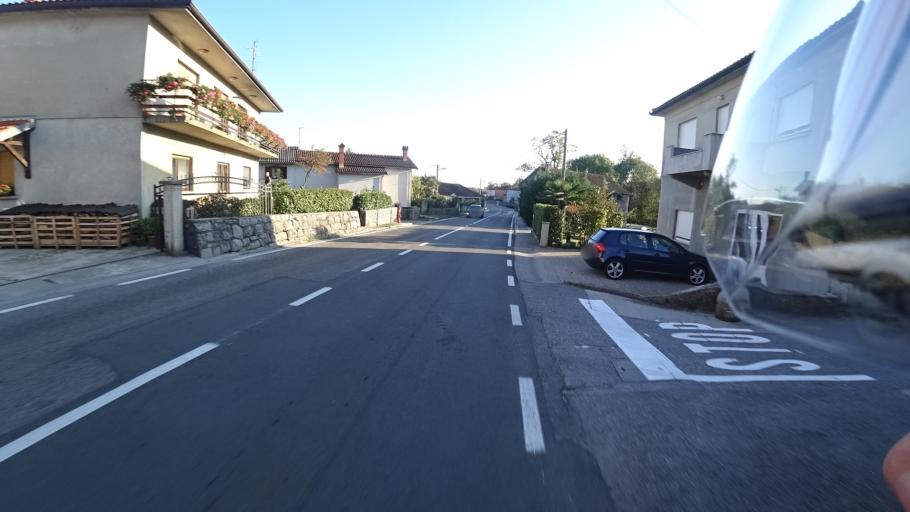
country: HR
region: Primorsko-Goranska
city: Matulji
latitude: 45.4013
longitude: 14.3078
